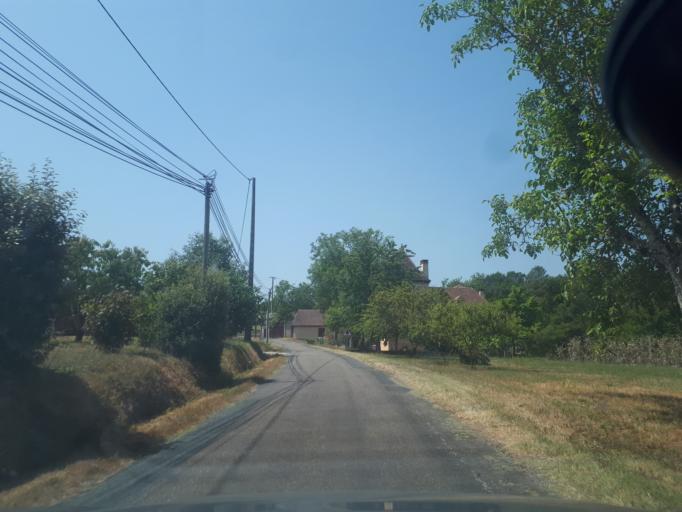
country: FR
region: Midi-Pyrenees
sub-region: Departement du Lot
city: Gourdon
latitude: 44.7660
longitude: 1.3551
